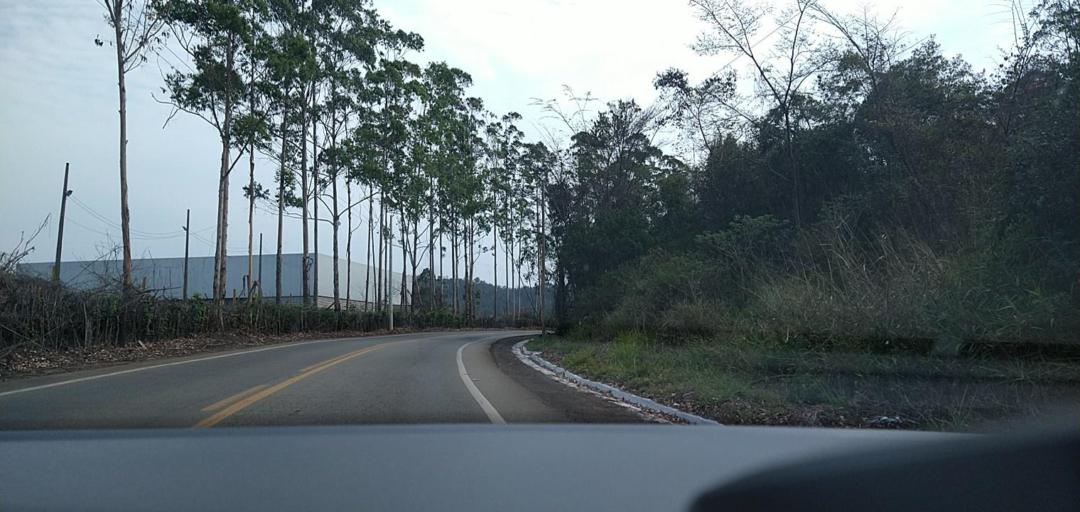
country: BR
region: Minas Gerais
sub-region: Rio Piracicaba
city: Rio Piracicaba
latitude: -19.8853
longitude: -43.1295
